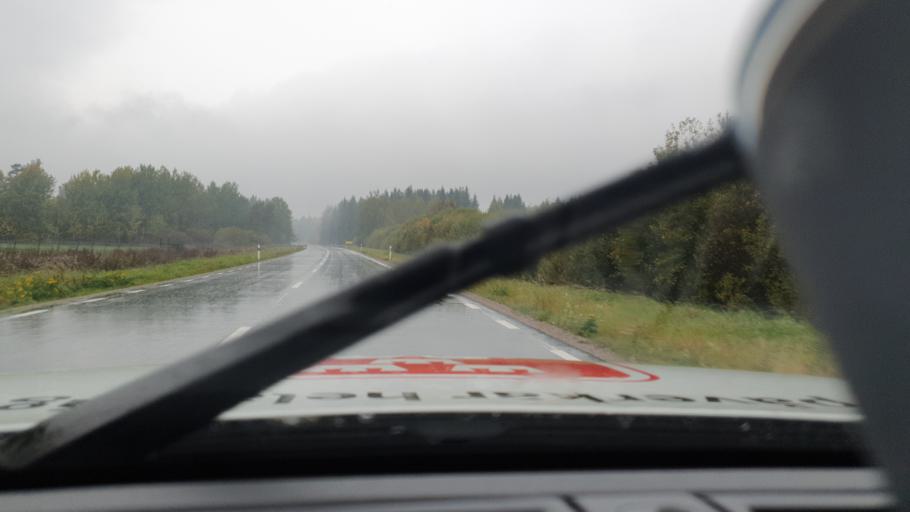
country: SE
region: Uppsala
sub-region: Tierps Kommun
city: Orbyhus
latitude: 60.2542
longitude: 17.6391
